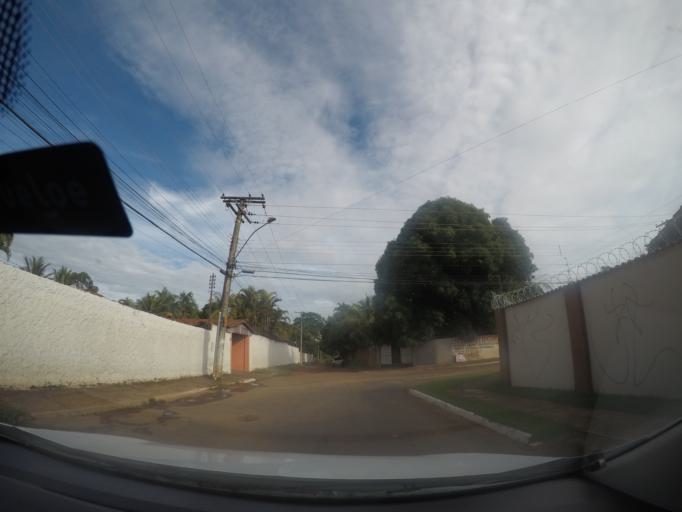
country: BR
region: Goias
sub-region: Goiania
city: Goiania
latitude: -16.6404
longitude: -49.3469
